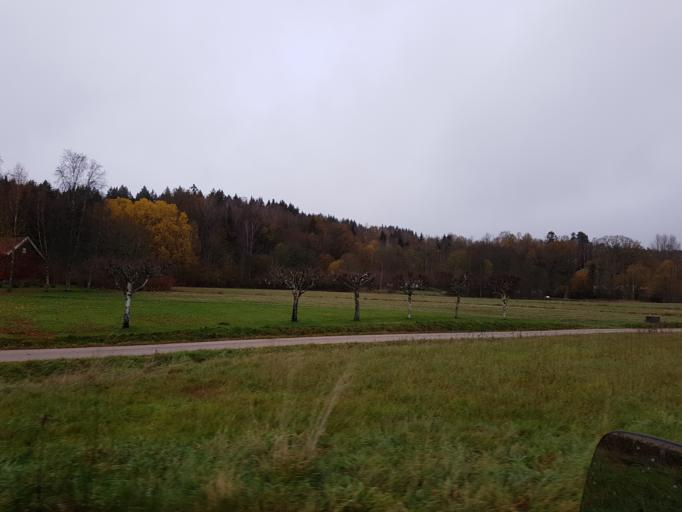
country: SE
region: Vaestra Goetaland
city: Svanesund
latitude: 58.1940
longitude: 11.8331
